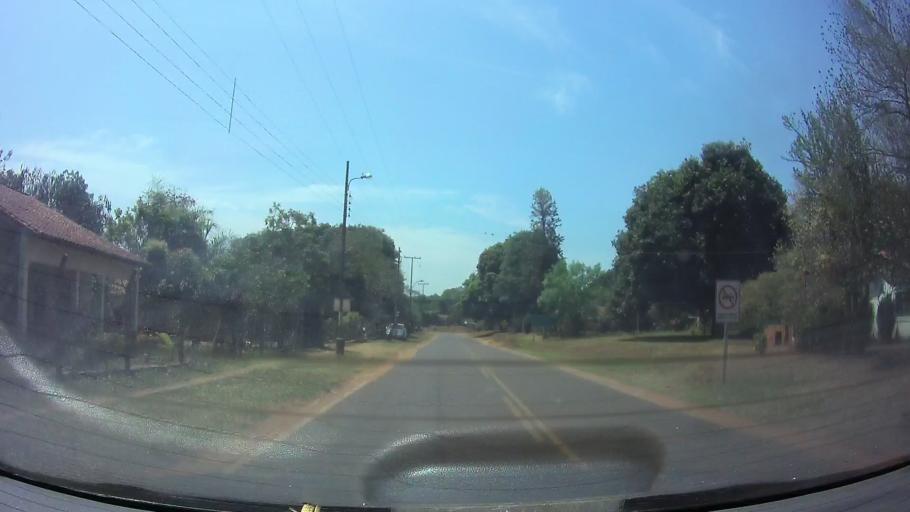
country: PY
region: Central
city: Ita
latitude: -25.4364
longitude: -57.3982
